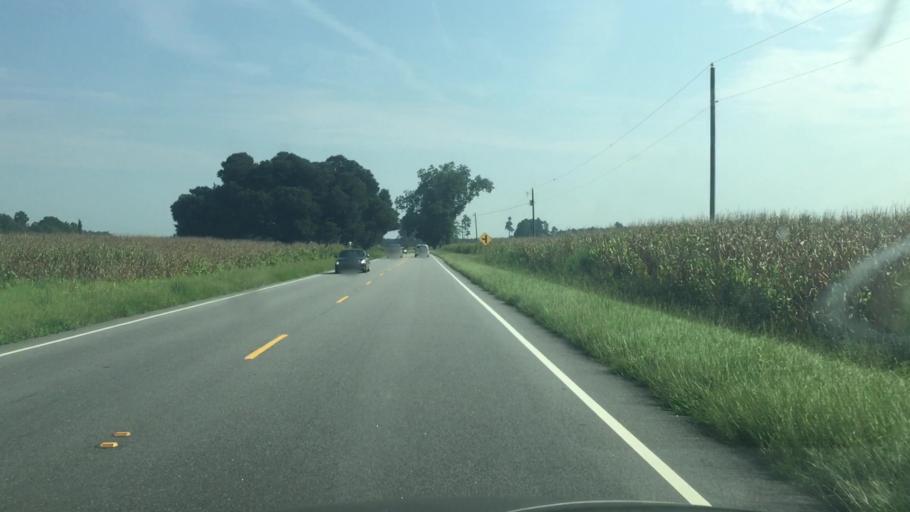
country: US
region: North Carolina
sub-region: Columbus County
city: Tabor City
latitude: 34.1677
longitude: -78.8437
